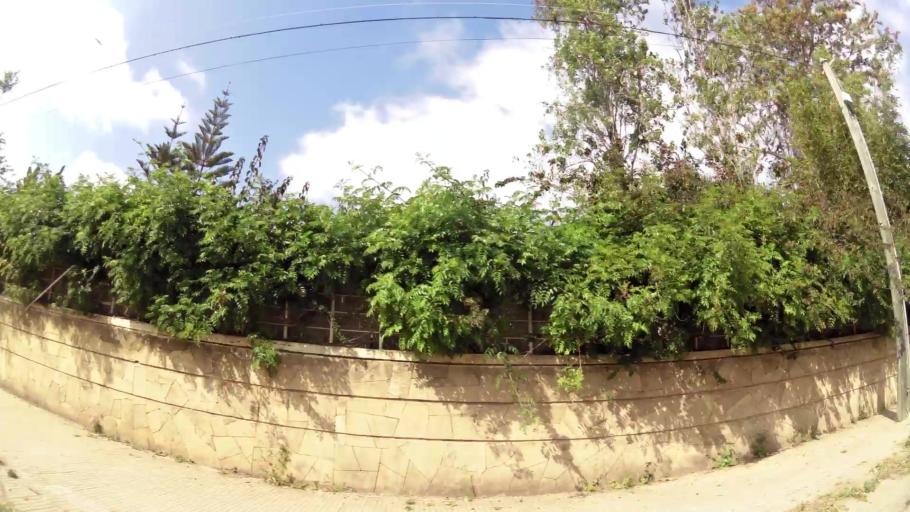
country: MA
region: Rabat-Sale-Zemmour-Zaer
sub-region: Rabat
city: Rabat
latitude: 33.9714
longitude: -6.8584
